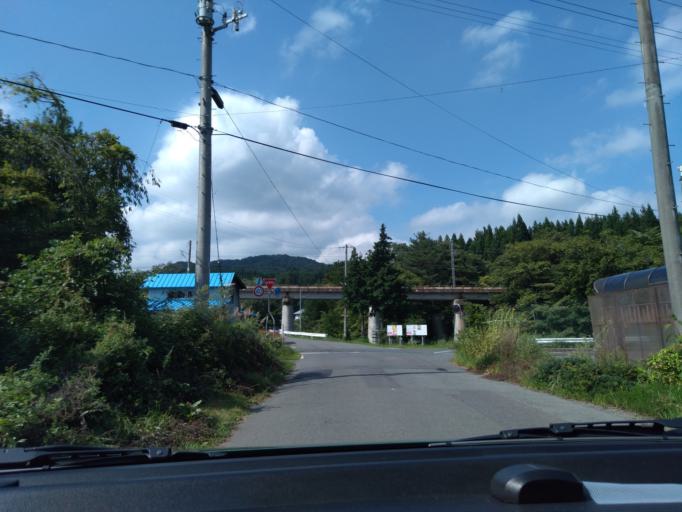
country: JP
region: Iwate
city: Shizukuishi
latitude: 39.6853
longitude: 140.9117
